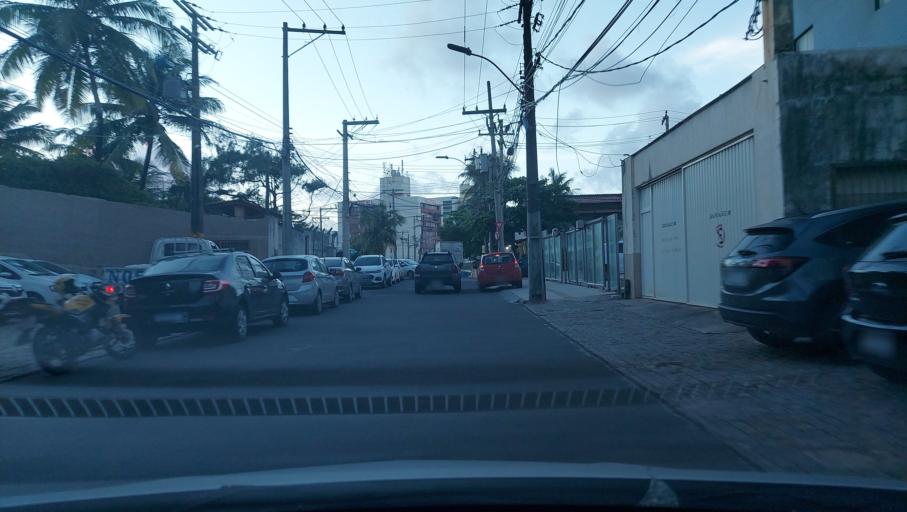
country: BR
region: Bahia
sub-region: Salvador
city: Salvador
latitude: -12.9862
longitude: -38.4364
